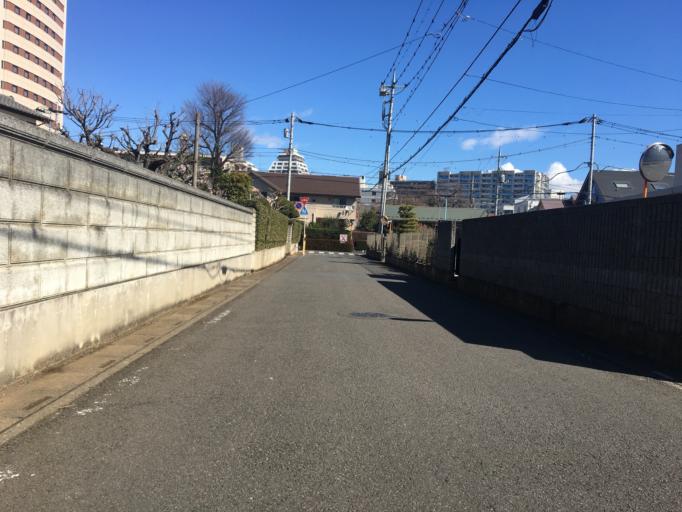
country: JP
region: Saitama
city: Shiki
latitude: 35.8177
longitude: 139.5736
